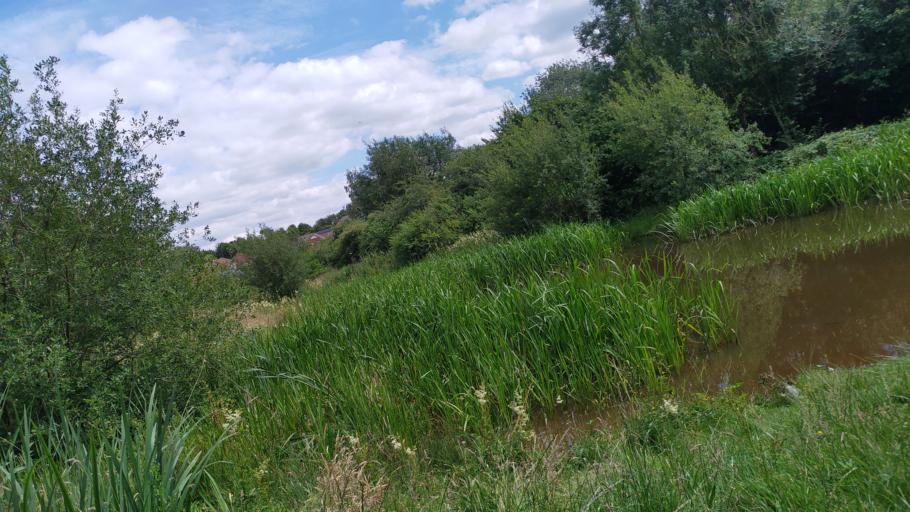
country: GB
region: England
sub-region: Lancashire
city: Coppull
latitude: 53.6341
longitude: -2.6411
